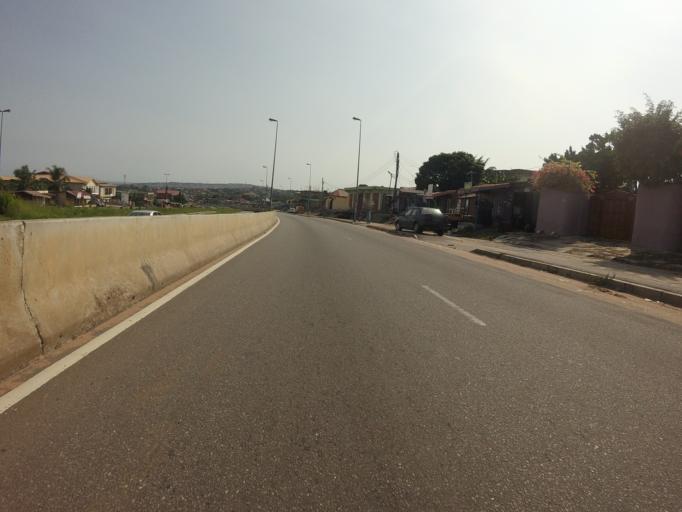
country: GH
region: Greater Accra
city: Gbawe
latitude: 5.6128
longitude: -0.2970
